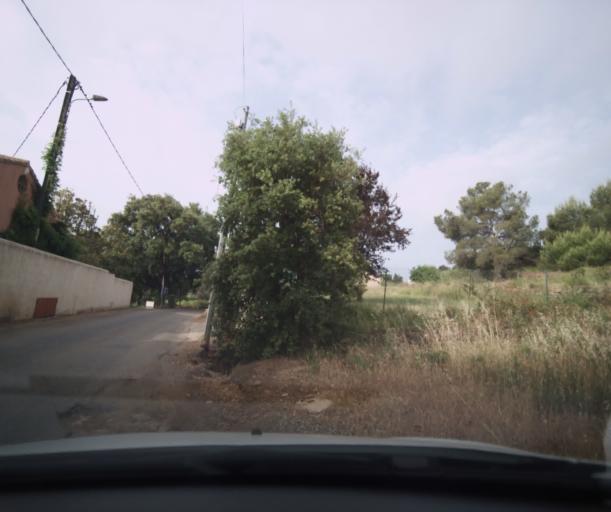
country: FR
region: Provence-Alpes-Cote d'Azur
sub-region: Departement du Var
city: Carqueiranne
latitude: 43.0883
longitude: 6.0555
